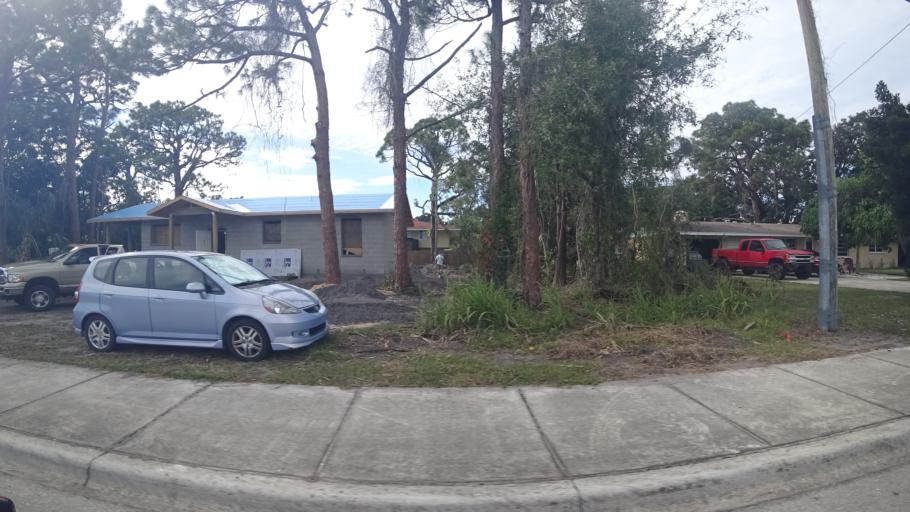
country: US
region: Florida
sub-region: Manatee County
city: West Bradenton
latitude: 27.4928
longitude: -82.6367
